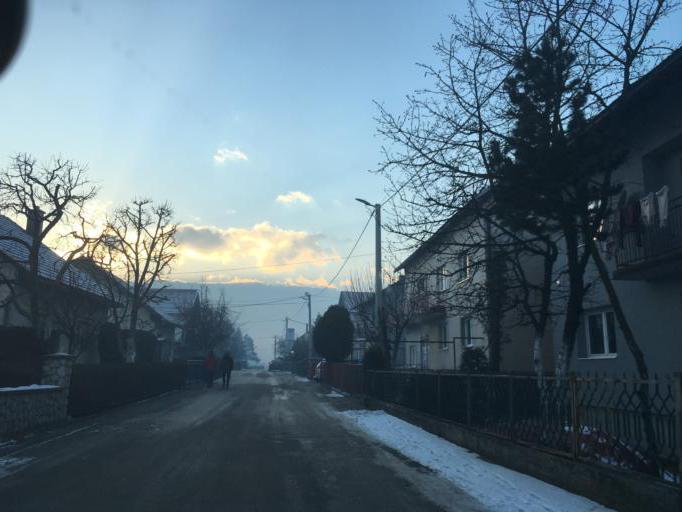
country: BA
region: Federation of Bosnia and Herzegovina
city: Bugojno
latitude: 44.0685
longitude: 17.4515
